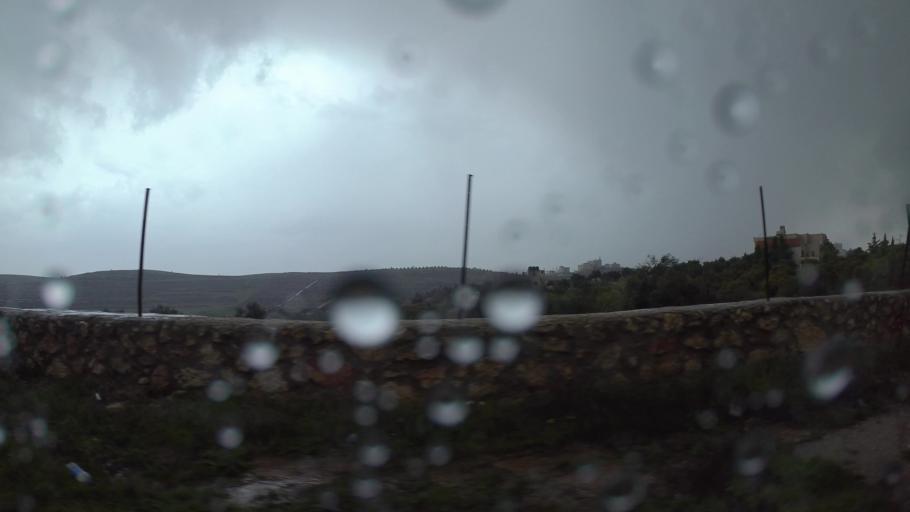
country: JO
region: Amman
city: Umm as Summaq
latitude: 31.8741
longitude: 35.8621
